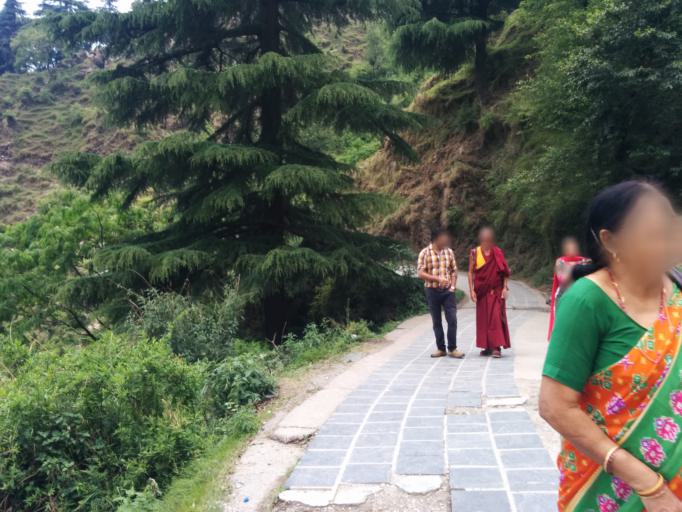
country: IN
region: Himachal Pradesh
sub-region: Kangra
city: Dharmsala
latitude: 32.2456
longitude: 76.3355
